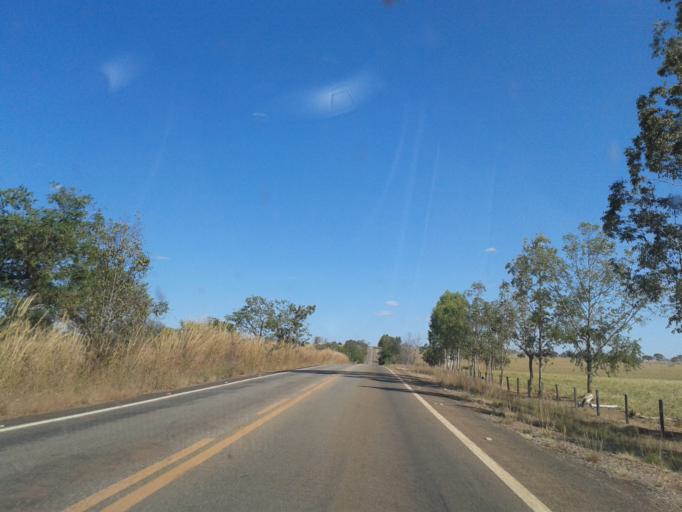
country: BR
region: Goias
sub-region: Crixas
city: Crixas
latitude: -14.2370
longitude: -50.3949
